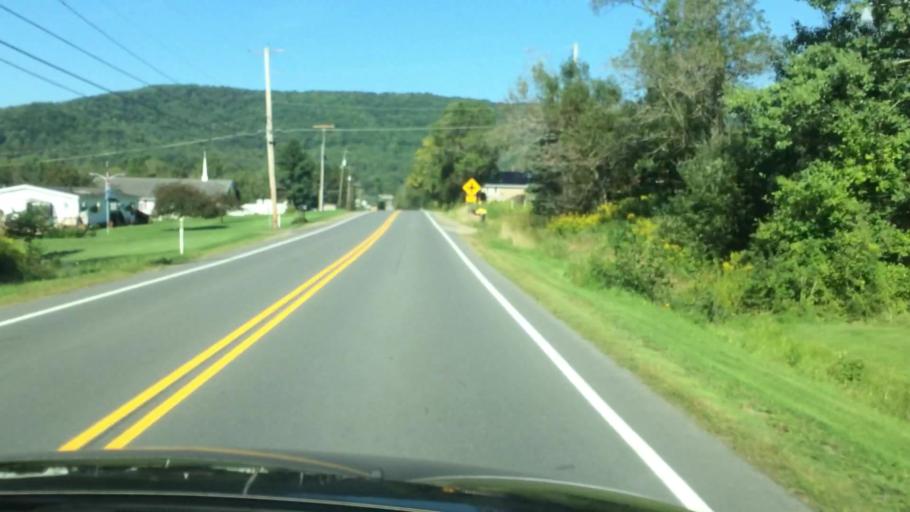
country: US
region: Pennsylvania
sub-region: McKean County
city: Bradford
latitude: 41.9124
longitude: -78.6391
